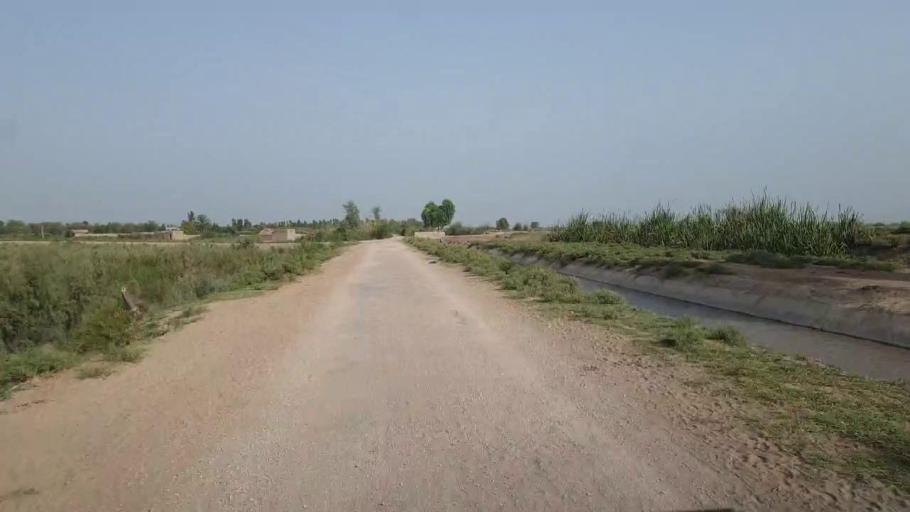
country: PK
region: Sindh
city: Daur
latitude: 26.3325
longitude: 68.1890
